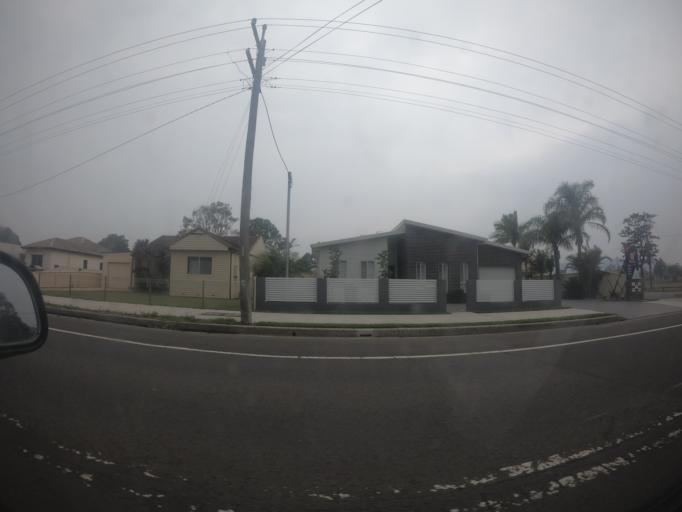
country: AU
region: New South Wales
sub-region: Shellharbour
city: Albion Park Rail
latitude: -34.5671
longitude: 150.7953
